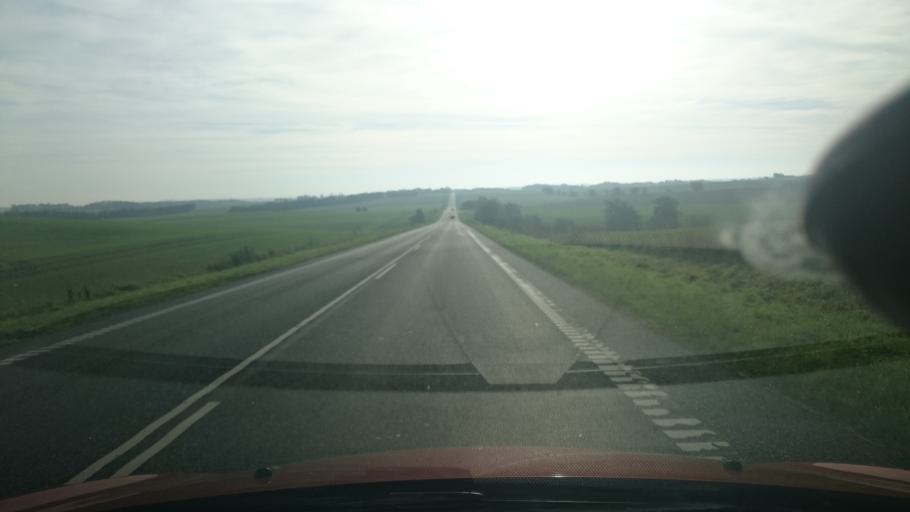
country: DK
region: Central Jutland
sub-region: Randers Kommune
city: Assentoft
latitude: 56.4234
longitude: 10.2057
